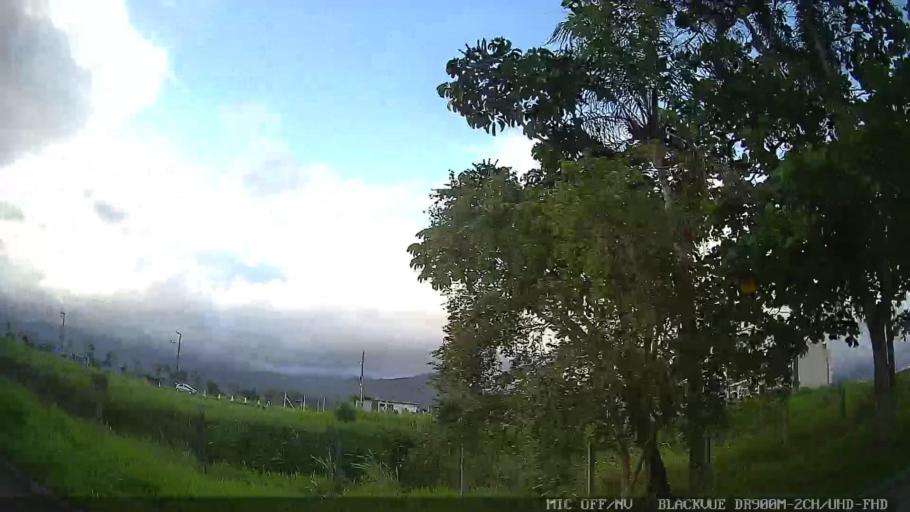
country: BR
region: Sao Paulo
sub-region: Caraguatatuba
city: Caraguatatuba
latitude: -23.6600
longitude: -45.4418
